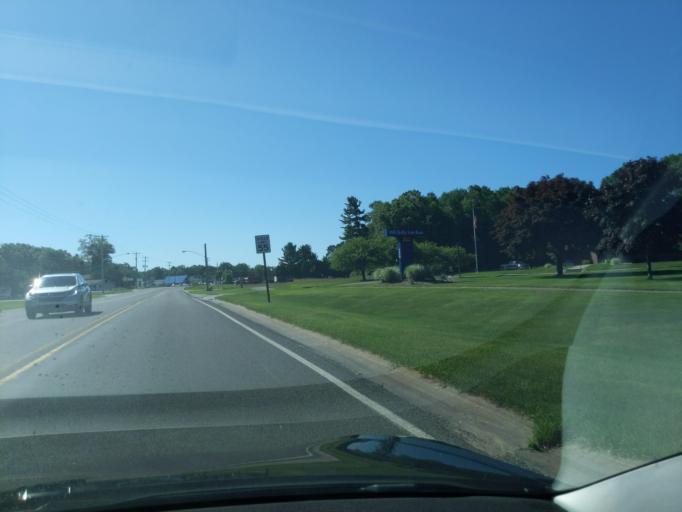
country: US
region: Michigan
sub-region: Muskegon County
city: Whitehall
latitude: 43.4087
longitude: -86.3173
